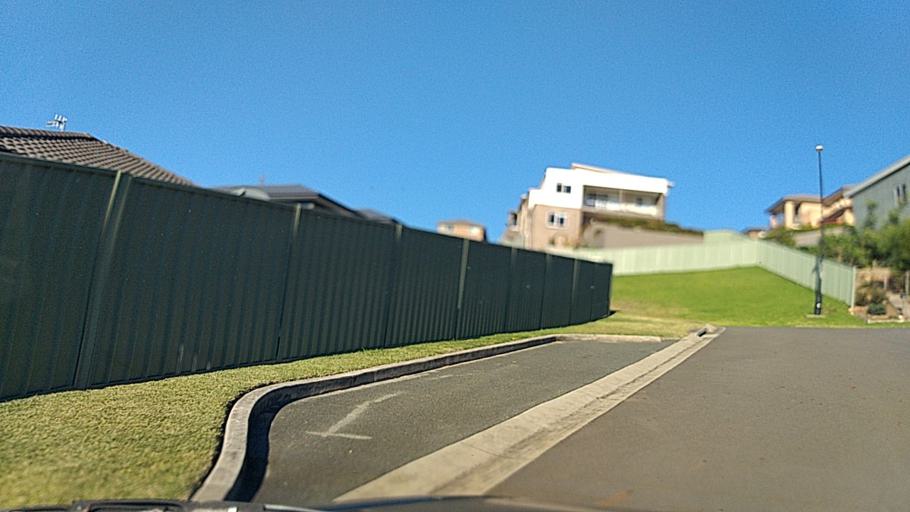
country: AU
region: New South Wales
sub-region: Wollongong
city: Cordeaux Heights
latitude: -34.4378
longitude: 150.8432
